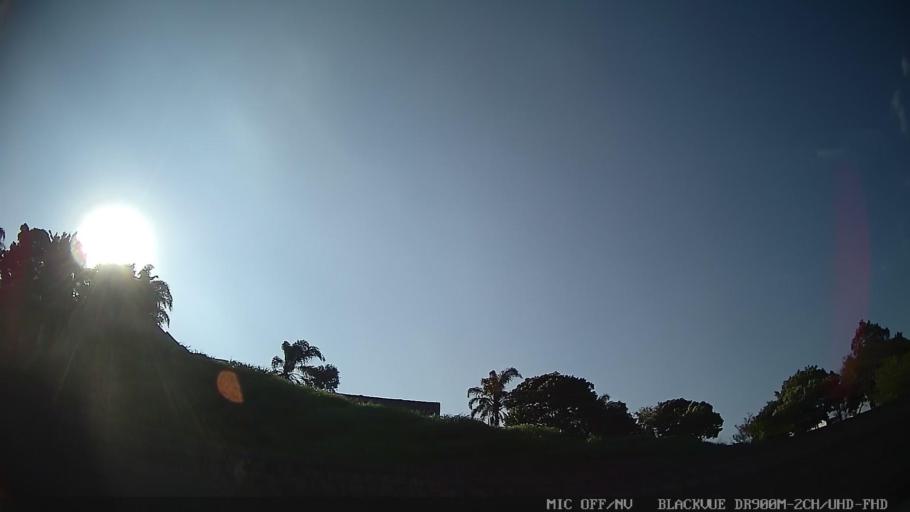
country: BR
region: Sao Paulo
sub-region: Ferraz De Vasconcelos
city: Ferraz de Vasconcelos
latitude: -23.5359
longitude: -46.4297
